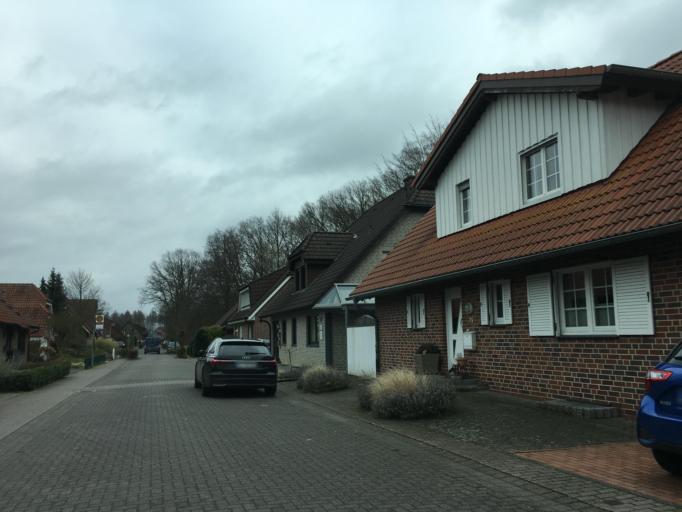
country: DE
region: North Rhine-Westphalia
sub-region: Regierungsbezirk Munster
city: Dulmen
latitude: 51.8390
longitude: 7.2966
